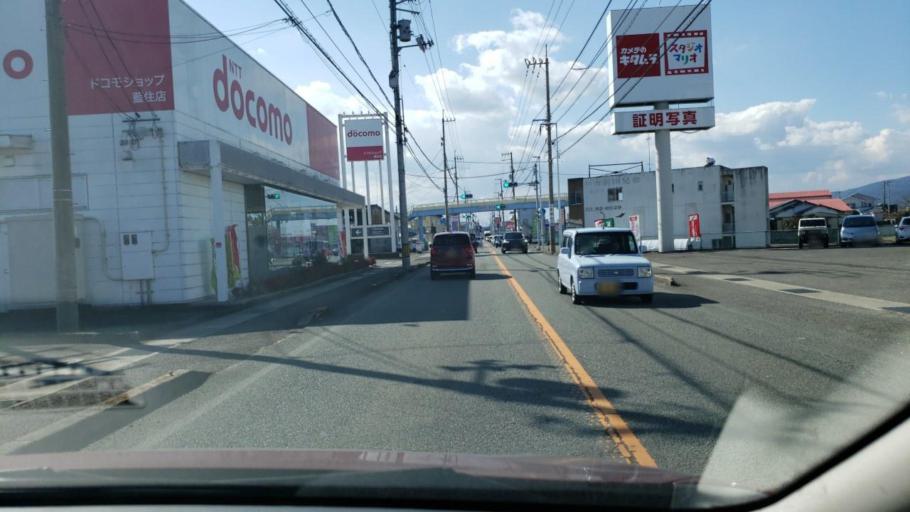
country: JP
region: Tokushima
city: Ishii
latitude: 34.1300
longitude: 134.4839
